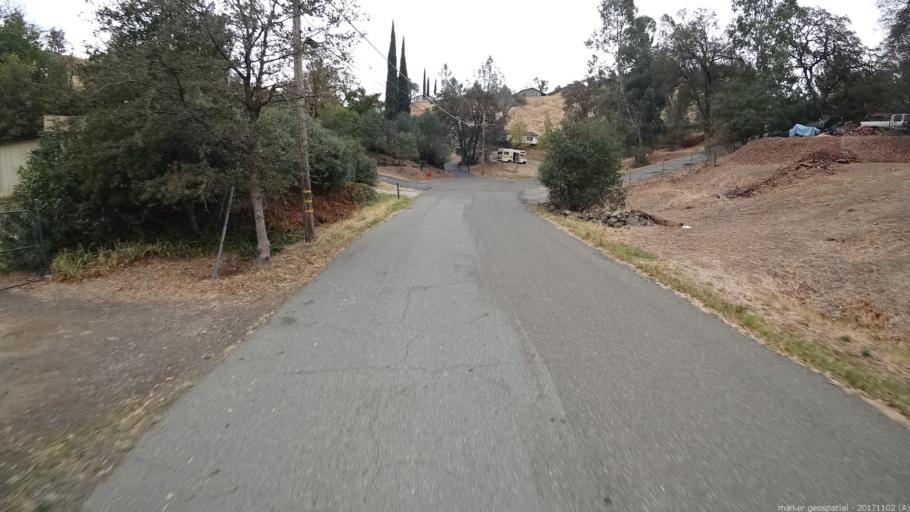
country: US
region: California
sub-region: Shasta County
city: Bella Vista
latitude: 40.7194
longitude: -122.2364
